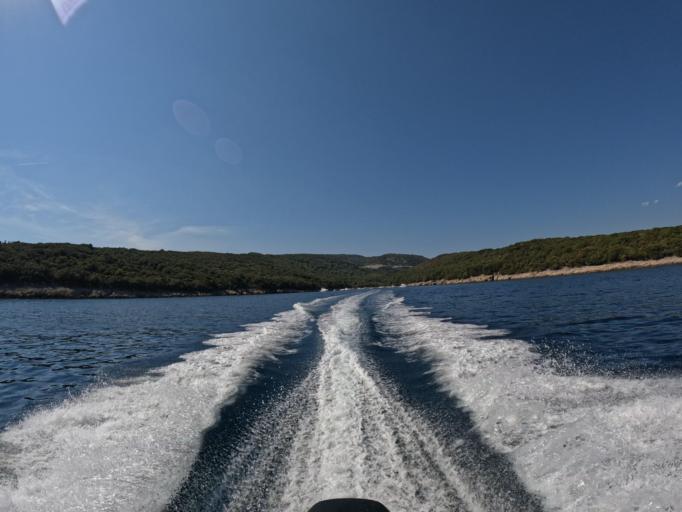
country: HR
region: Primorsko-Goranska
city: Cres
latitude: 44.9472
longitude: 14.4664
